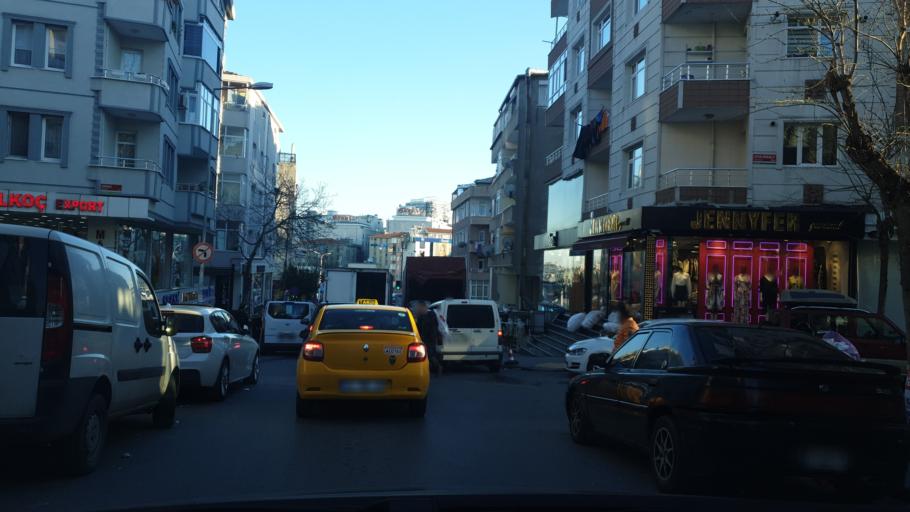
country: TR
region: Istanbul
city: merter keresteciler
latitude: 41.0169
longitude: 28.8762
